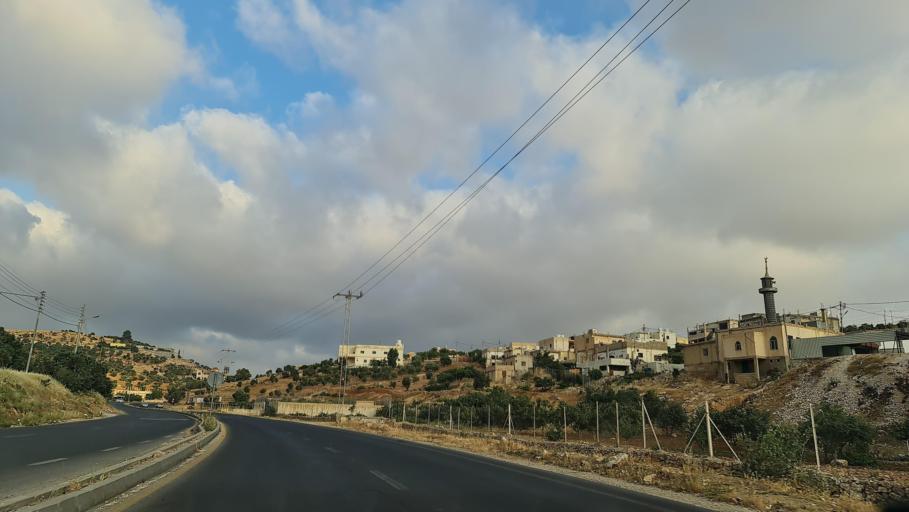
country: JO
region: Amman
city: Al Jubayhah
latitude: 32.0922
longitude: 35.9466
